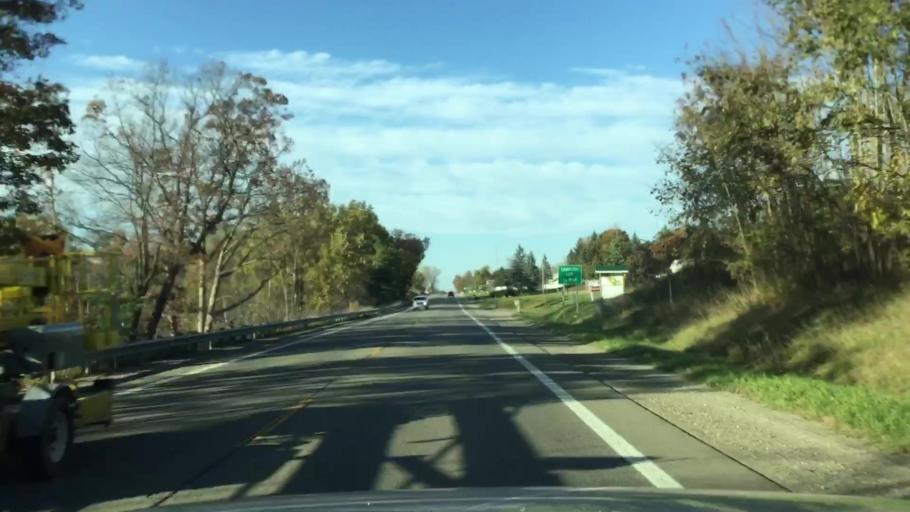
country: US
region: Michigan
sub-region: Lapeer County
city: Barnes Lake-Millers Lake
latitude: 43.1847
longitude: -83.3124
